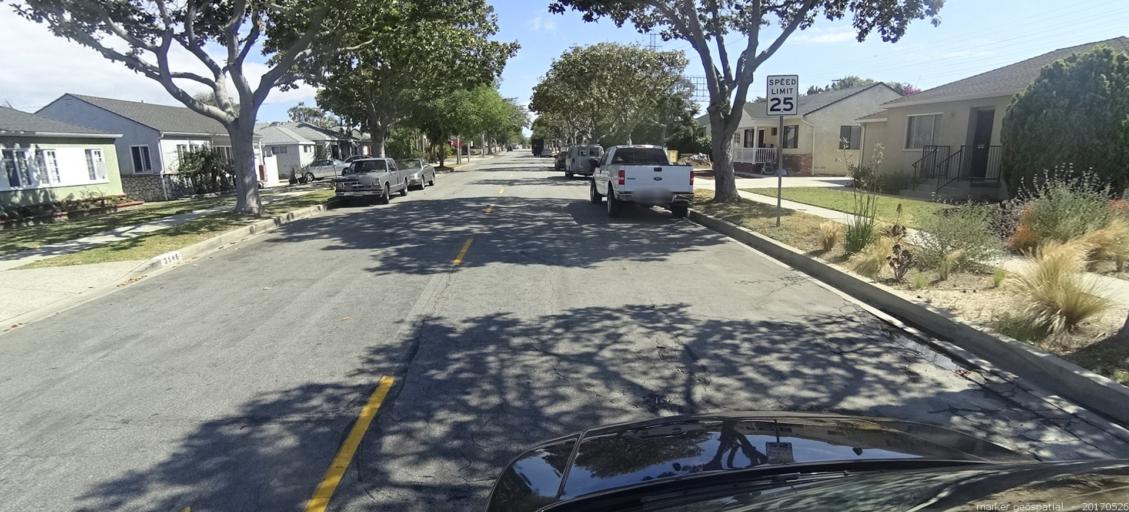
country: US
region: California
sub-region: Los Angeles County
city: Lawndale
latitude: 33.8870
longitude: -118.3652
